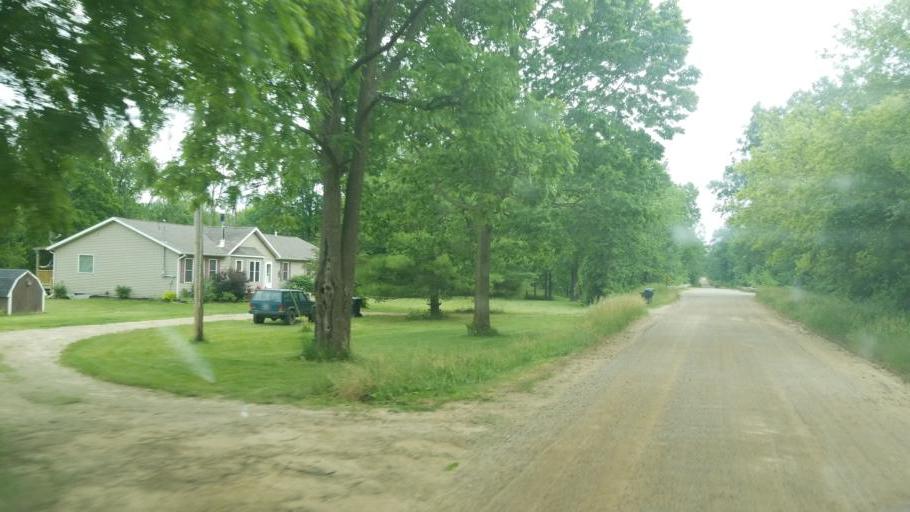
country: US
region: Michigan
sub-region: Barry County
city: Nashville
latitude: 42.6208
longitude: -84.9757
